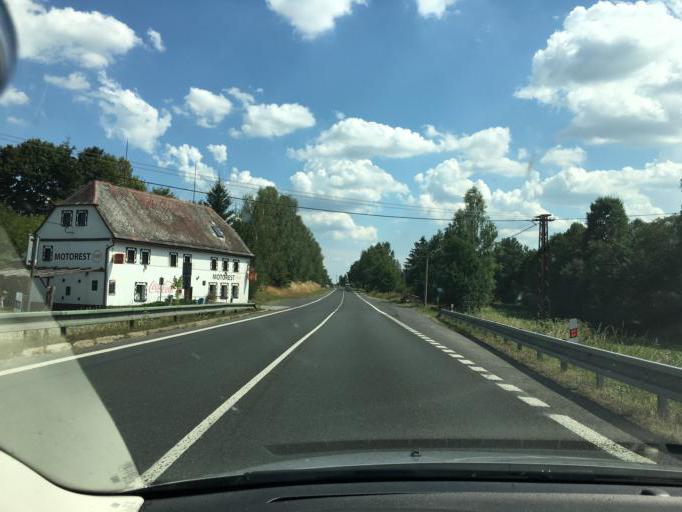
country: CZ
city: Jablonne v Podjestedi
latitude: 50.7734
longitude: 14.7236
